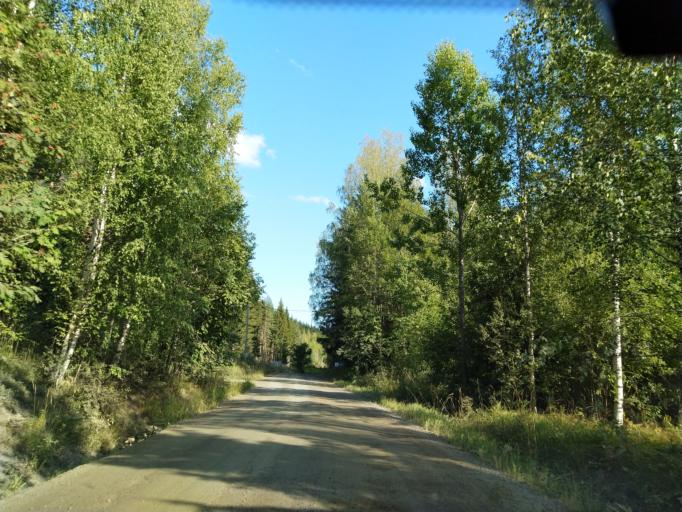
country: FI
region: Central Finland
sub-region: Jaemsae
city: Kuhmoinen
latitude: 61.7082
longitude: 24.9133
